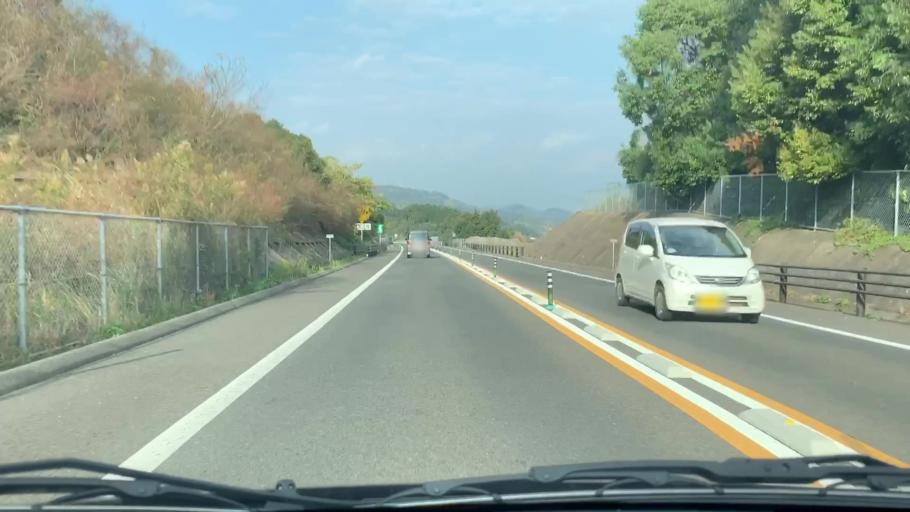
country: JP
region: Nagasaki
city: Sasebo
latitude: 33.0094
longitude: 129.7289
